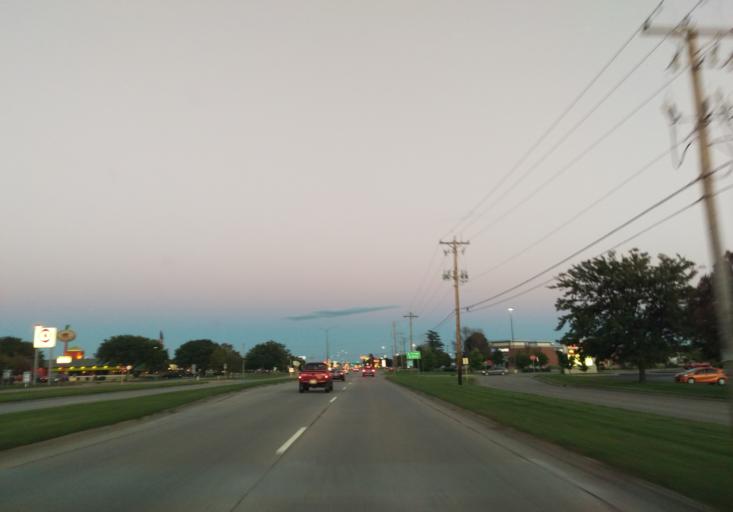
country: US
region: Wisconsin
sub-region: Rock County
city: Janesville
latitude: 42.7209
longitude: -88.9999
